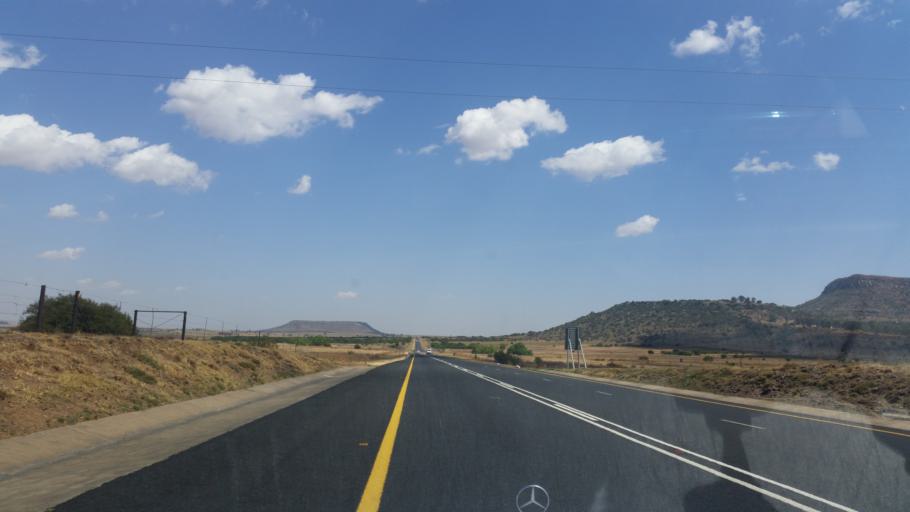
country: ZA
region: Orange Free State
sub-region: Thabo Mofutsanyana District Municipality
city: Senekal
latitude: -28.3011
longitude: 27.7894
